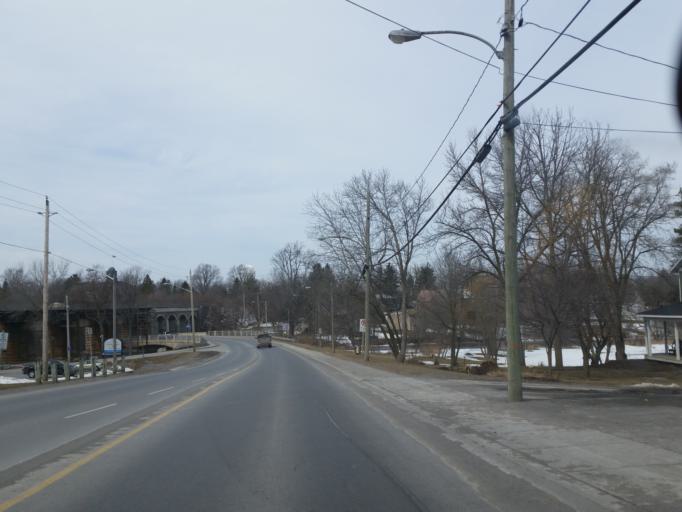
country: CA
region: Ontario
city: Skatepark
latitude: 44.2512
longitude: -76.9435
